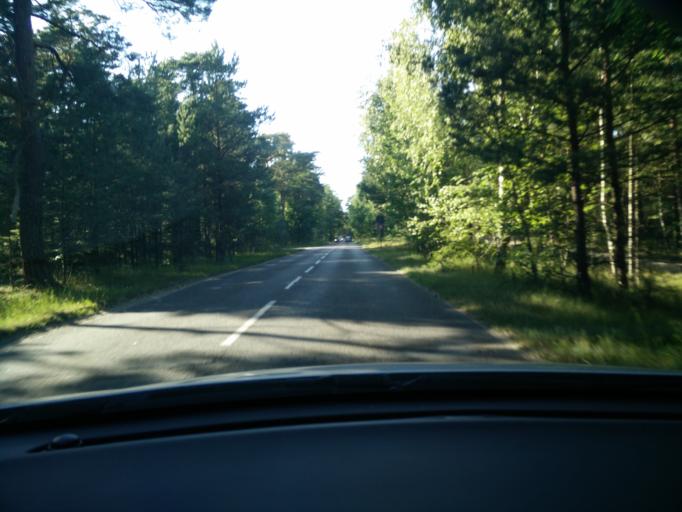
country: PL
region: Pomeranian Voivodeship
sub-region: Powiat pucki
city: Hel
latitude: 54.6292
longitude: 18.7890
